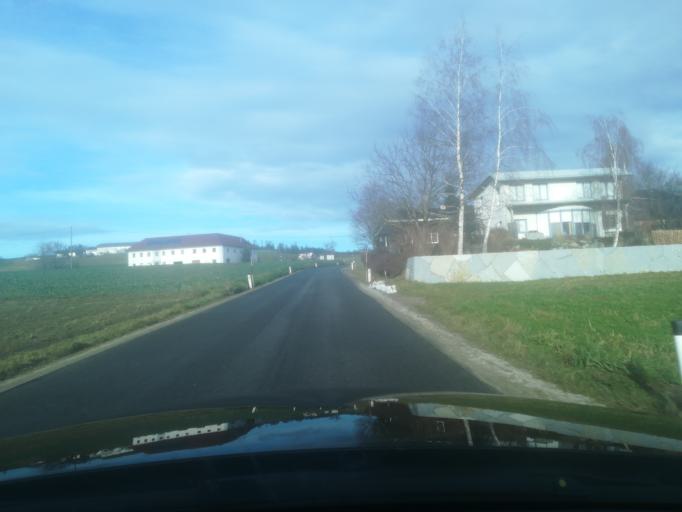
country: AT
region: Upper Austria
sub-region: Politischer Bezirk Perg
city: Perg
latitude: 48.3402
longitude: 14.6210
